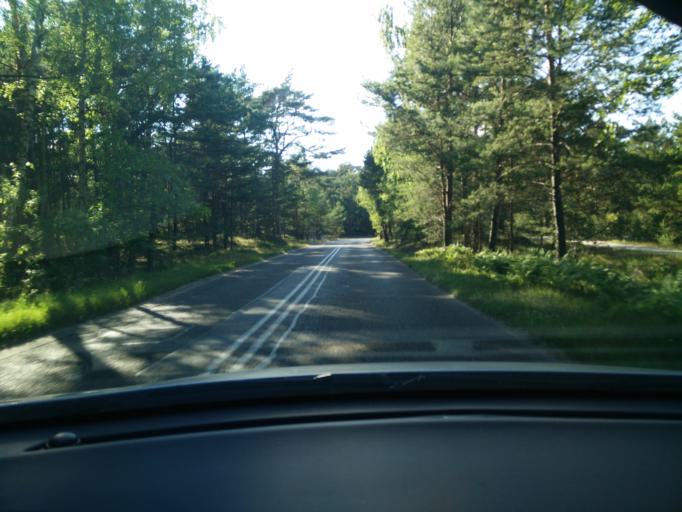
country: PL
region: Pomeranian Voivodeship
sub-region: Powiat pucki
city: Hel
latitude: 54.6279
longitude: 18.7916
